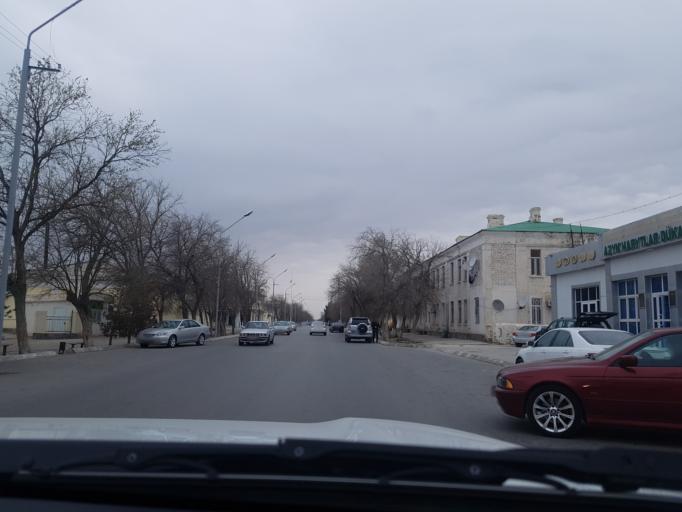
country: TM
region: Balkan
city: Balkanabat
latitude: 39.5028
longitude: 54.3655
